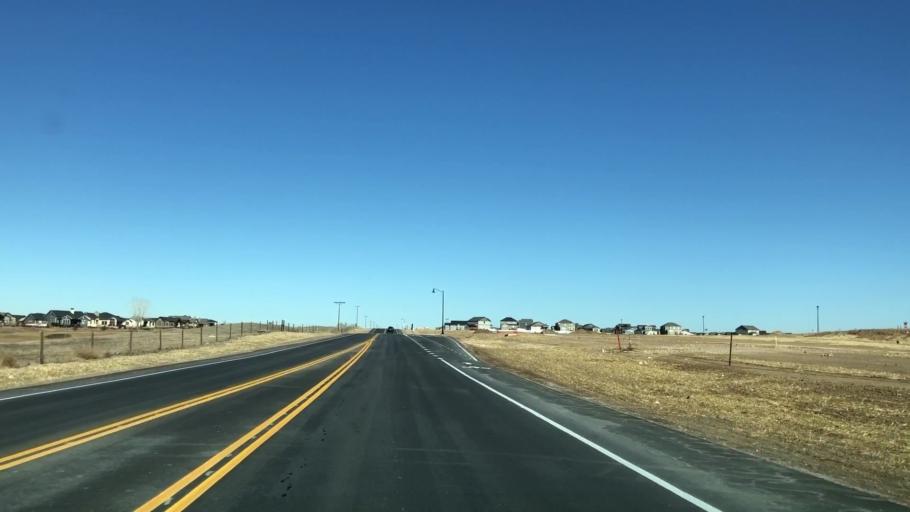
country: US
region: Colorado
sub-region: Weld County
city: Windsor
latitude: 40.5248
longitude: -104.9442
